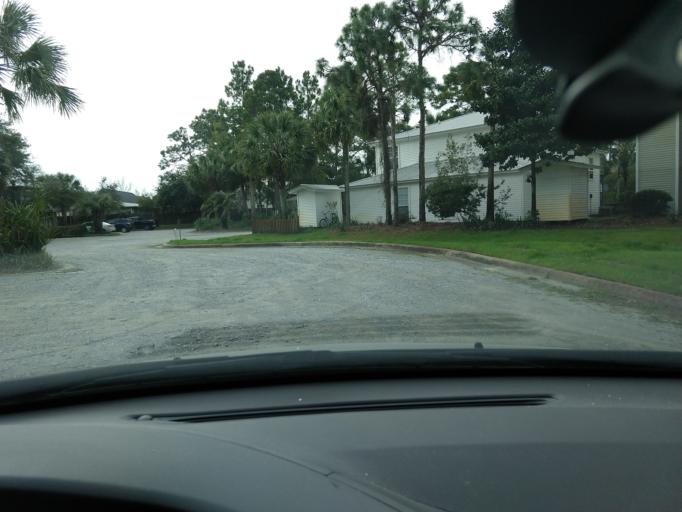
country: US
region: Florida
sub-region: Walton County
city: Miramar Beach
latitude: 30.3920
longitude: -86.3076
